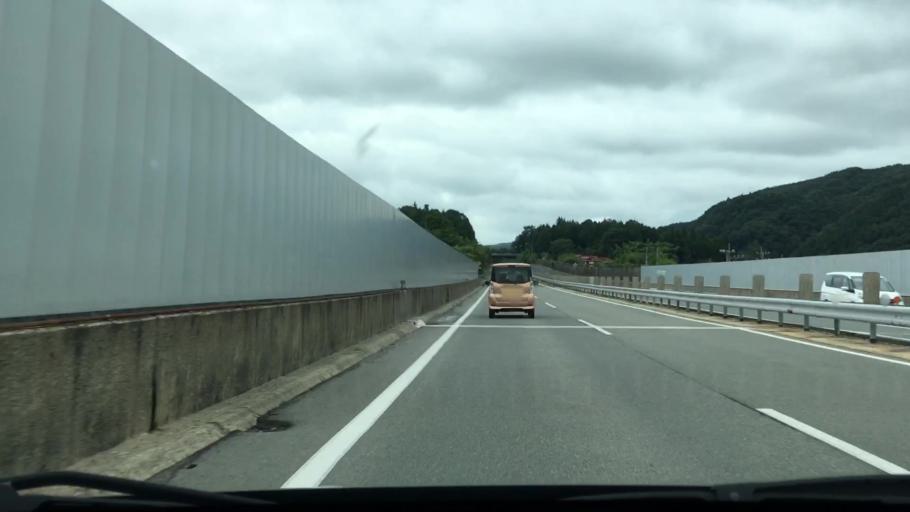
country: JP
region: Hiroshima
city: Miyoshi
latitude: 34.7712
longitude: 132.8213
